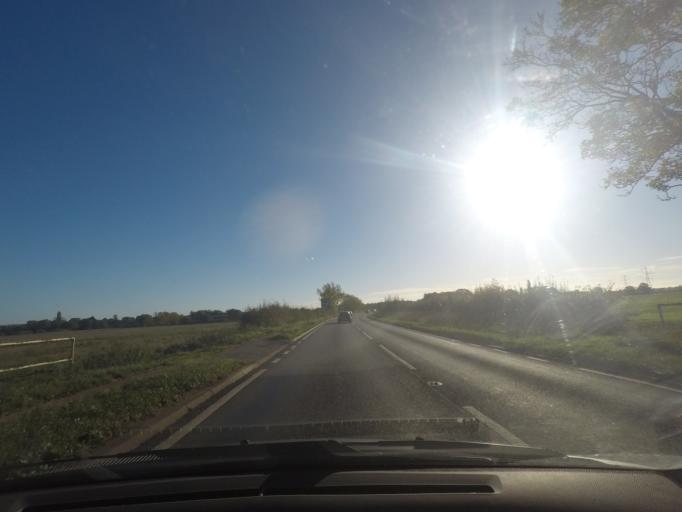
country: GB
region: England
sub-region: East Riding of Yorkshire
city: Wilberfoss
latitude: 53.9440
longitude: -0.8704
